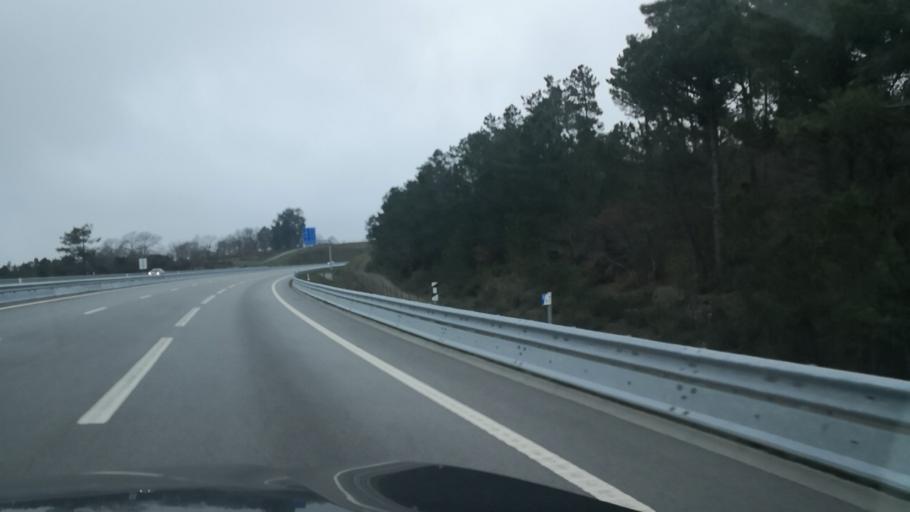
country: PT
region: Vila Real
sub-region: Santa Marta de Penaguiao
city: Santa Marta de Penaguiao
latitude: 41.2670
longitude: -7.8114
